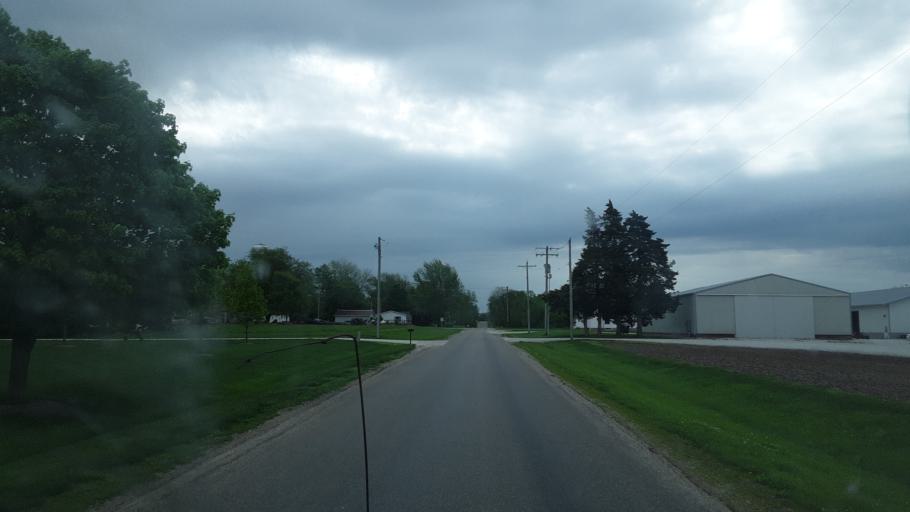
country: US
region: Illinois
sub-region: Fulton County
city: Astoria
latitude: 40.3642
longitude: -90.4326
